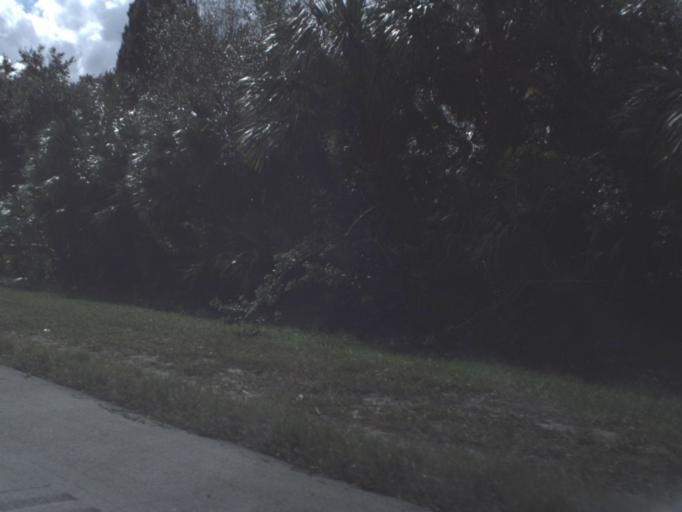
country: US
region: Florida
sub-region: Brevard County
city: Port Saint John
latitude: 28.4499
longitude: -80.8732
